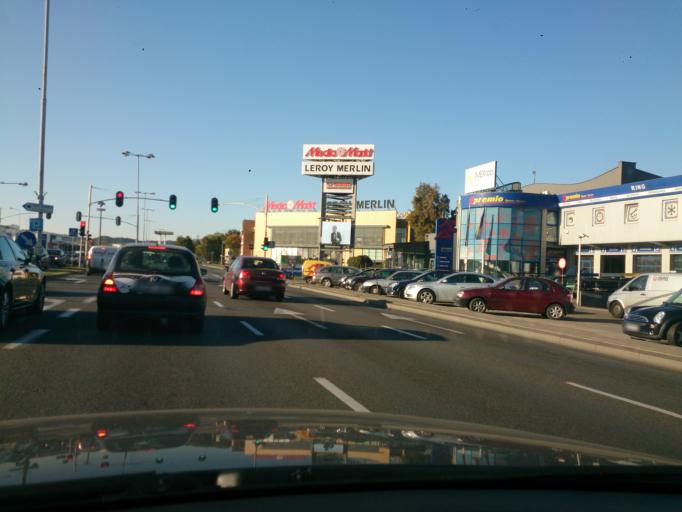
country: PL
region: Pomeranian Voivodeship
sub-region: Sopot
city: Sopot
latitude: 54.3931
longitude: 18.5827
